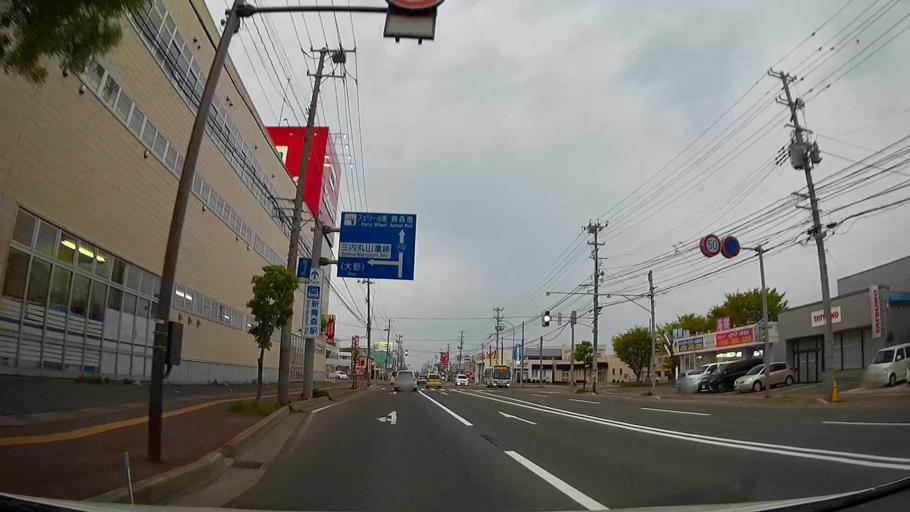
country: JP
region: Aomori
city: Aomori Shi
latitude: 40.8043
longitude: 140.7557
